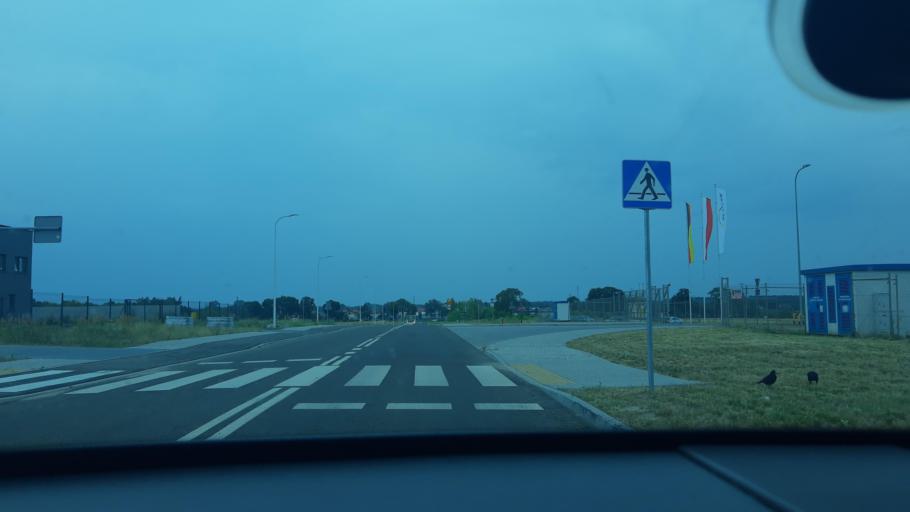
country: PL
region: Lodz Voivodeship
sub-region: Powiat sieradzki
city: Sieradz
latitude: 51.5738
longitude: 18.6992
